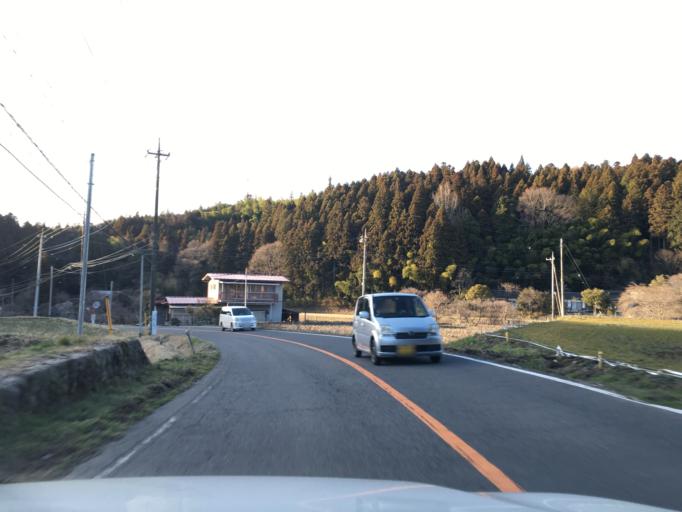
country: JP
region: Tochigi
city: Otawara
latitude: 36.8609
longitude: 140.1730
